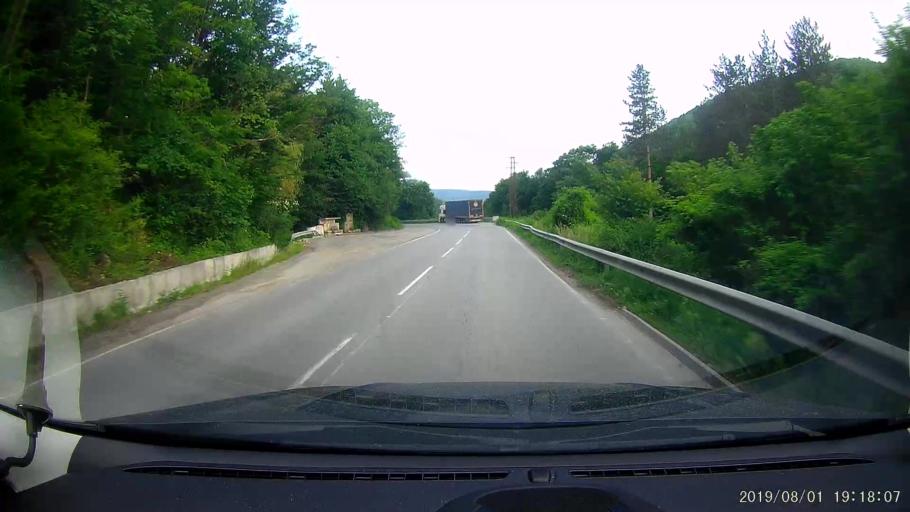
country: BG
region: Shumen
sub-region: Obshtina Smyadovo
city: Smyadovo
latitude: 42.9167
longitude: 26.9386
